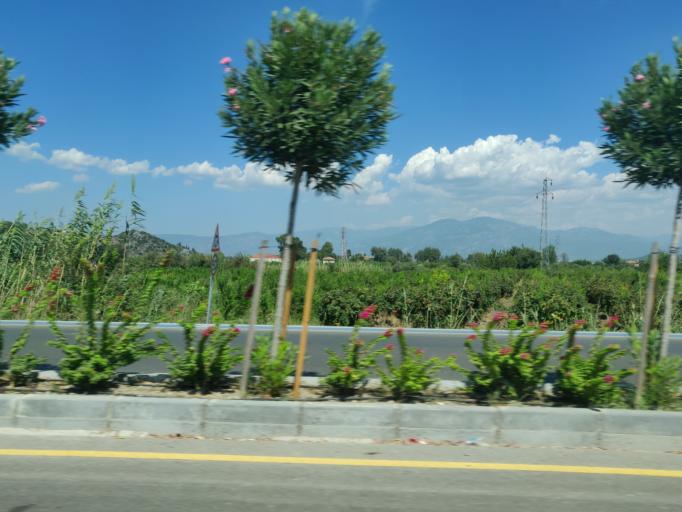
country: TR
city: Dalyan
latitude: 36.8407
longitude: 28.6544
